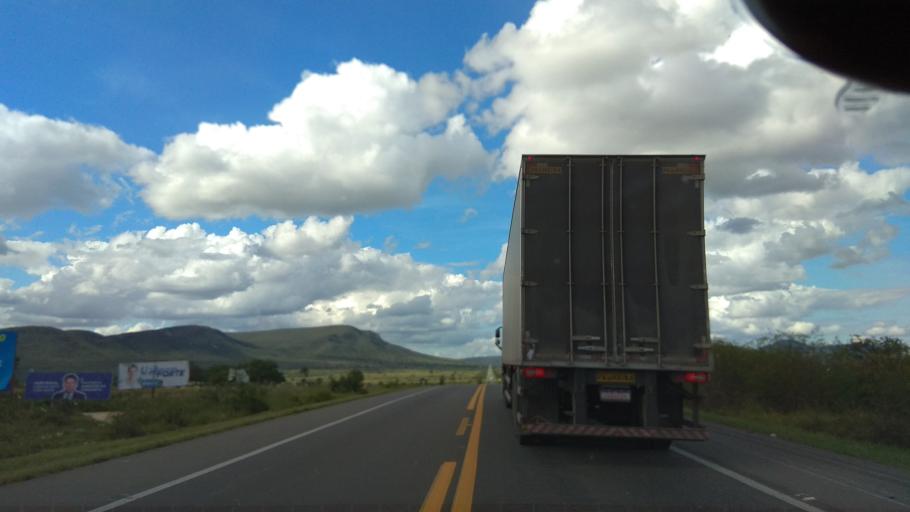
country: BR
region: Bahia
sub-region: Castro Alves
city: Castro Alves
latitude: -12.6743
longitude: -39.6579
